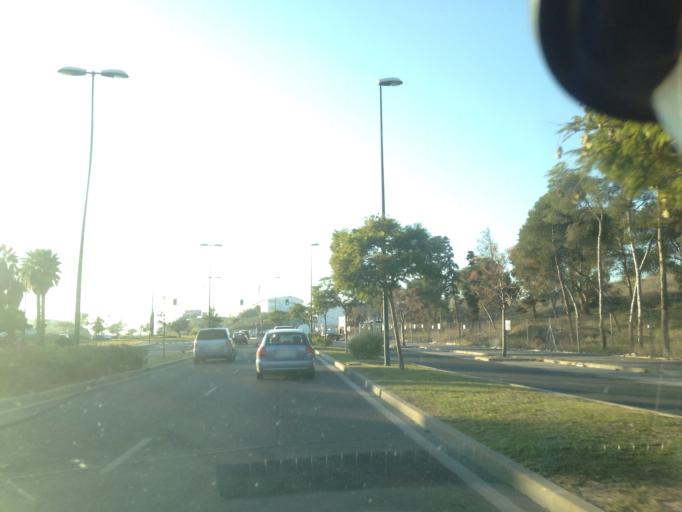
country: ES
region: Andalusia
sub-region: Provincia de Malaga
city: Malaga
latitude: 36.7082
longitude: -4.4804
